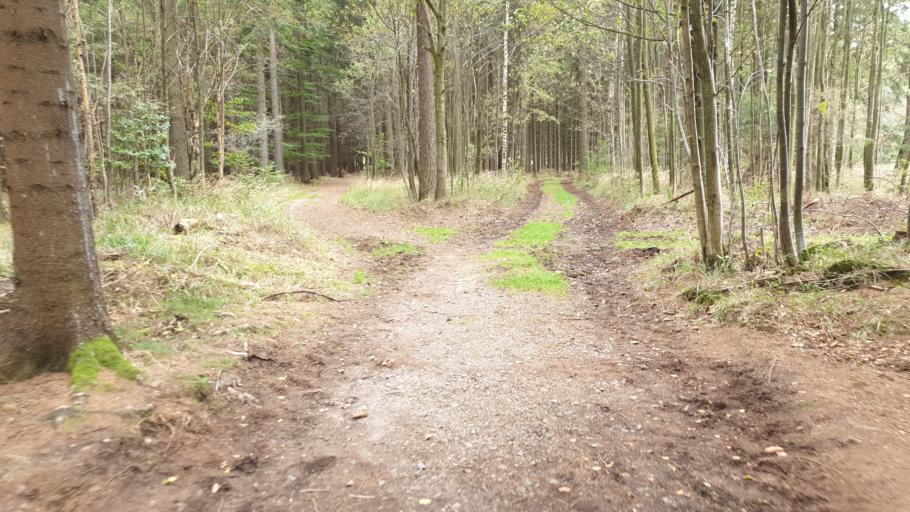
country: DE
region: Saxony
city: Pobershau
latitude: 50.6348
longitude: 13.2382
